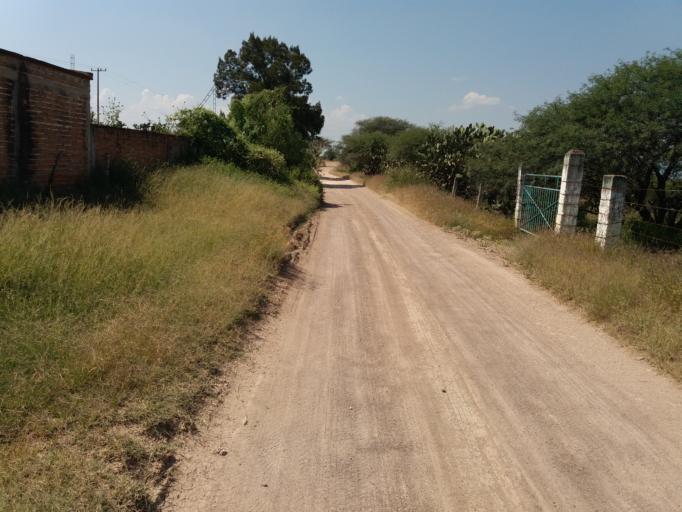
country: MX
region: Aguascalientes
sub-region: Aguascalientes
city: Penuelas (El Cienegal)
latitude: 21.7604
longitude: -102.2723
